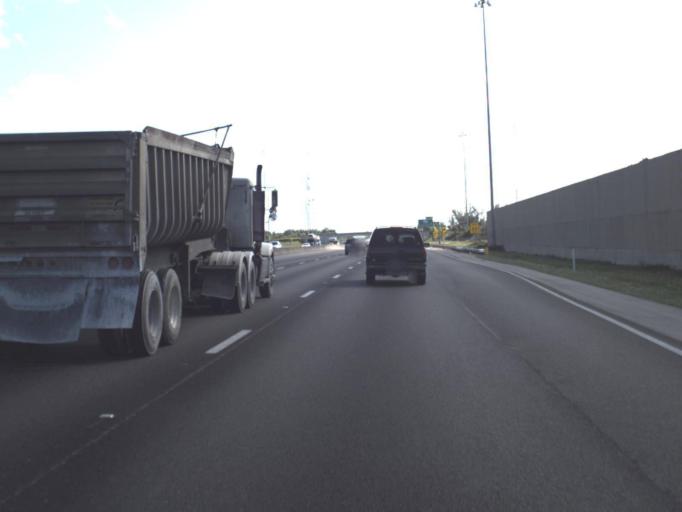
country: US
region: Florida
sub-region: Palm Beach County
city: Boca Del Mar
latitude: 26.3802
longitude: -80.1711
